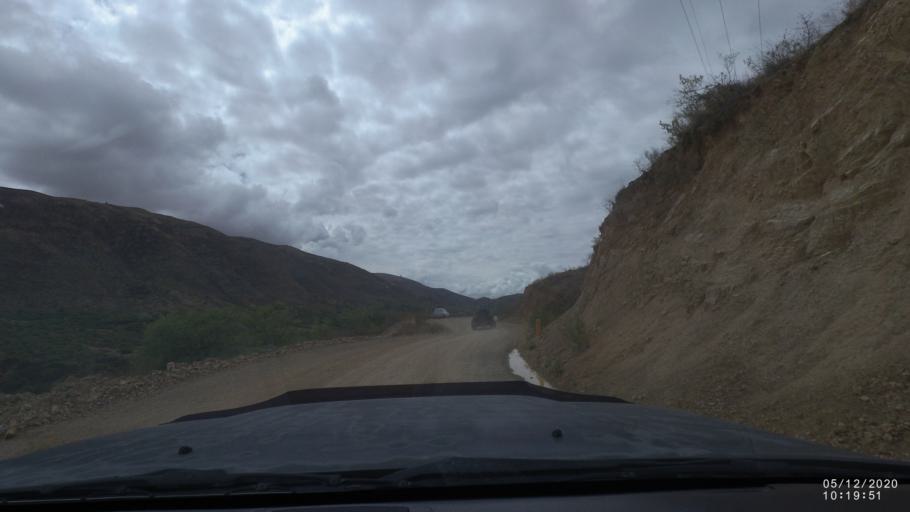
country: BO
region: Cochabamba
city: Sipe Sipe
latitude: -17.4805
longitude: -66.2833
